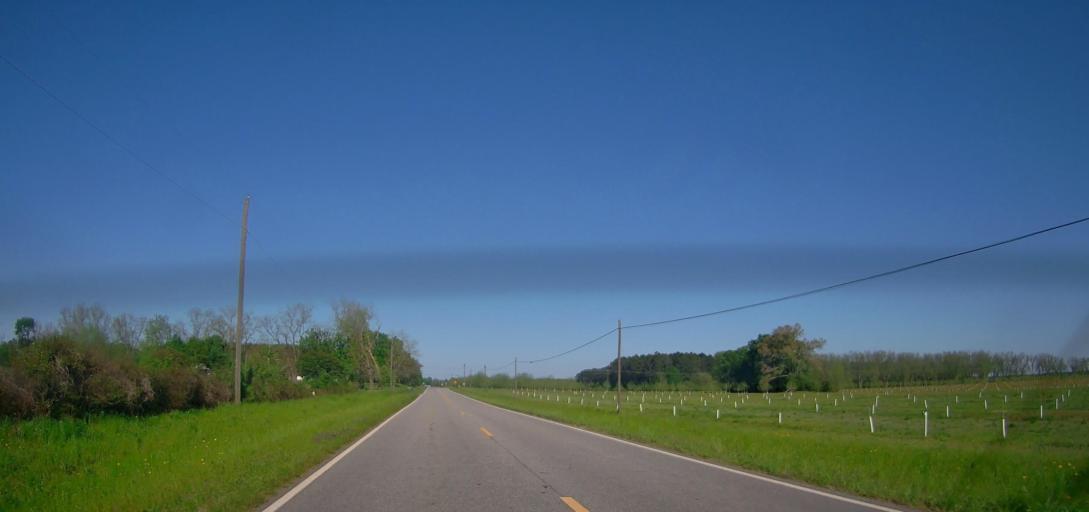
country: US
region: Georgia
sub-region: Houston County
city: Perry
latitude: 32.4515
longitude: -83.6571
